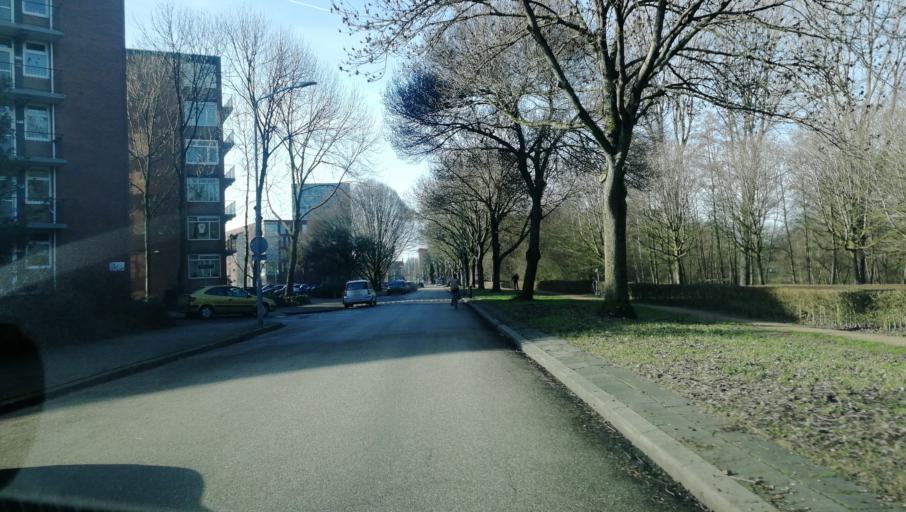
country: NL
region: Limburg
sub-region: Gemeente Venlo
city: Venlo
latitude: 51.3728
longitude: 6.1899
